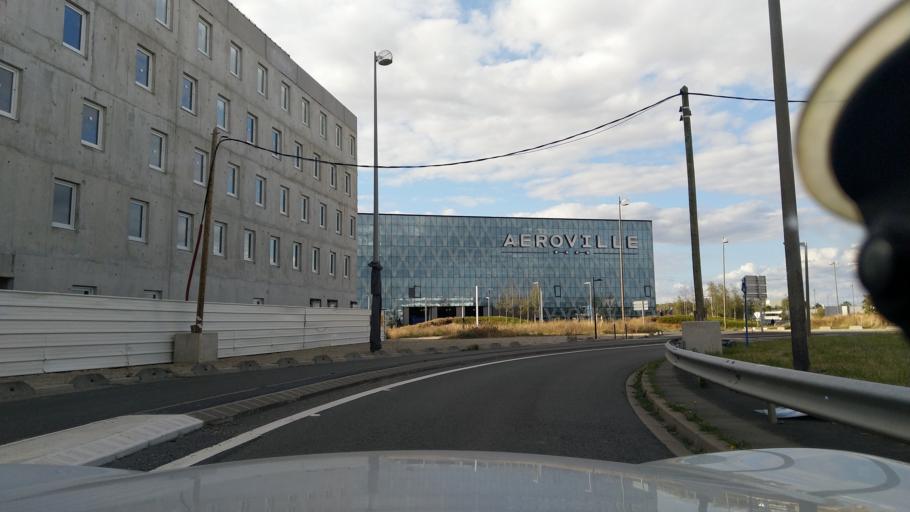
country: FR
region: Ile-de-France
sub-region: Departement du Val-d'Oise
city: Roissy-en-France
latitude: 48.9886
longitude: 2.5239
